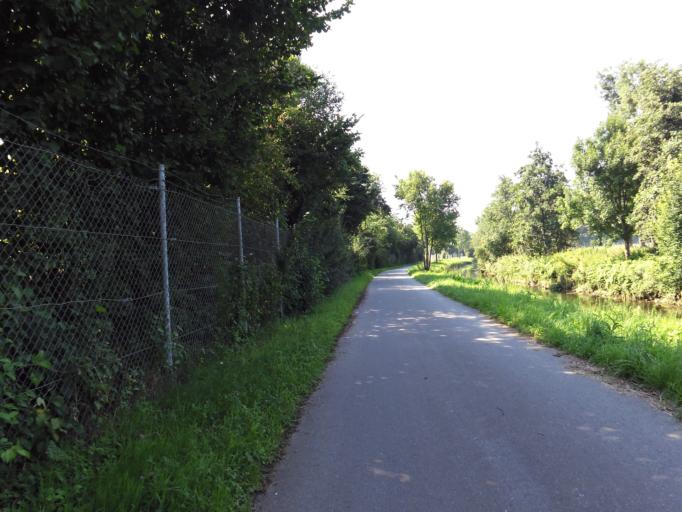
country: DE
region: North Rhine-Westphalia
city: Geilenkirchen
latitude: 51.0056
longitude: 6.1752
